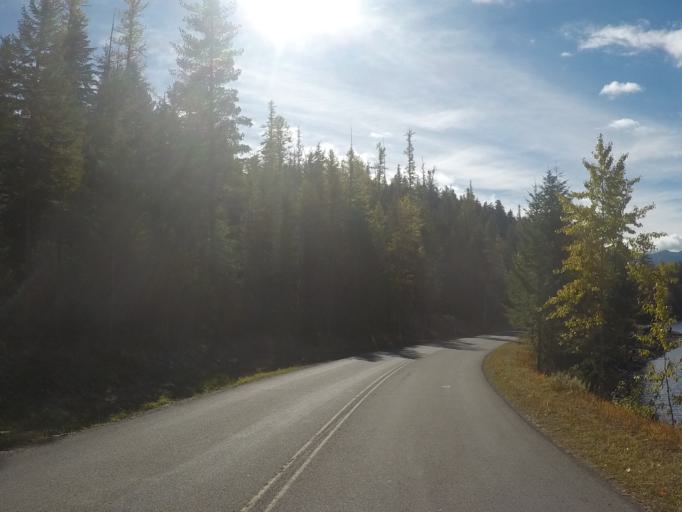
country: US
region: Montana
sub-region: Flathead County
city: Columbia Falls
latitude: 48.6108
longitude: -113.8817
